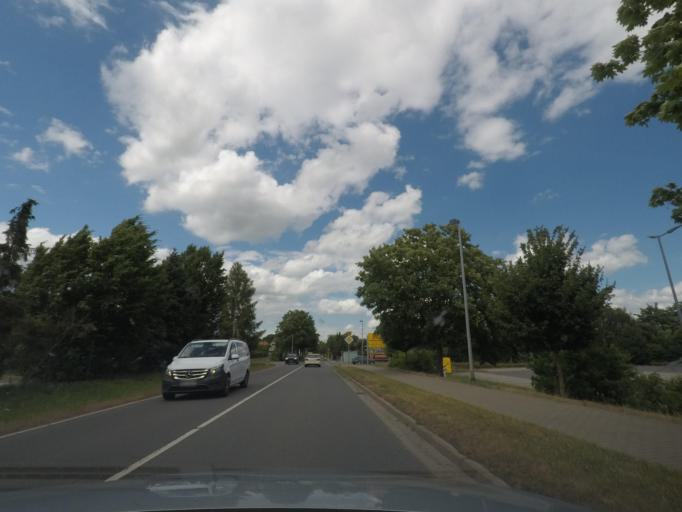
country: DE
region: Saxony-Anhalt
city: Schwanebeck
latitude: 51.9613
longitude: 11.1215
